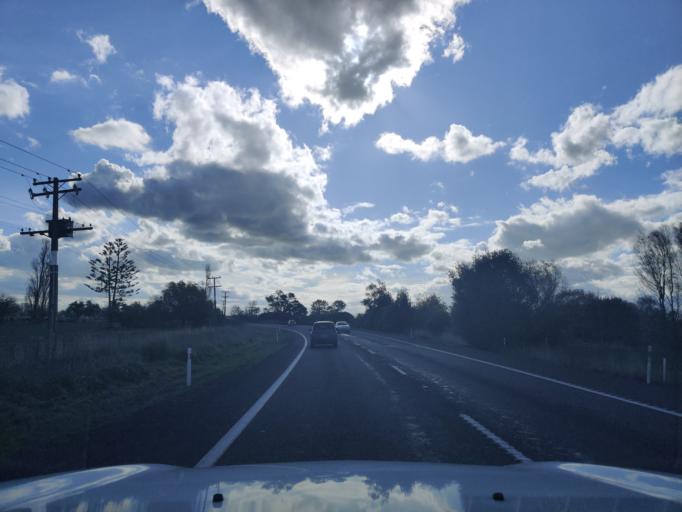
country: NZ
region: Waikato
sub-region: Hauraki District
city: Ngatea
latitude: -37.2858
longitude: 175.5464
